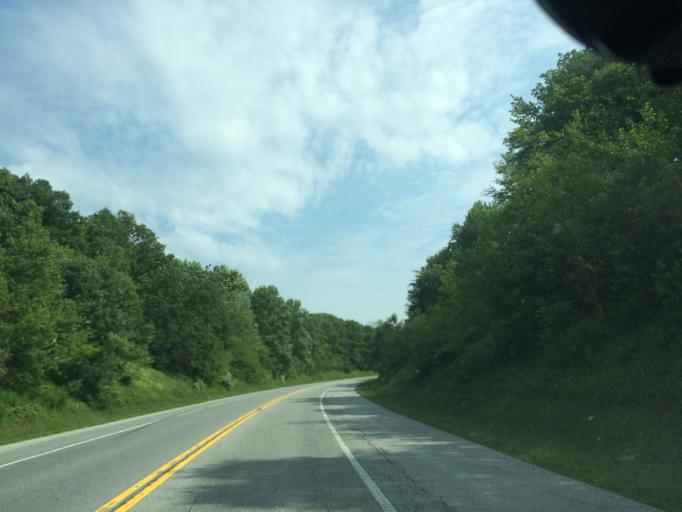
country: US
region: Maryland
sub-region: Carroll County
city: Westminster
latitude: 39.5132
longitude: -76.9945
